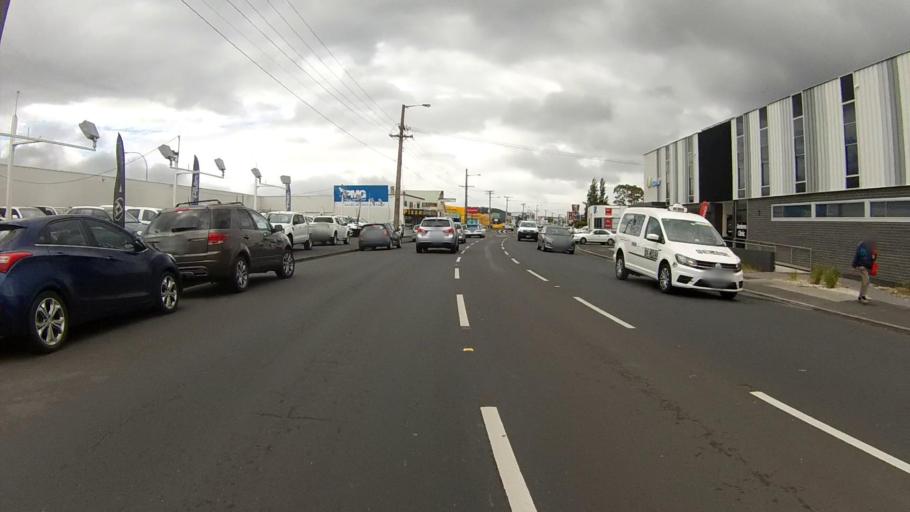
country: AU
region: Tasmania
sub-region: Glenorchy
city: Goodwood
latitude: -42.8362
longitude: 147.2869
